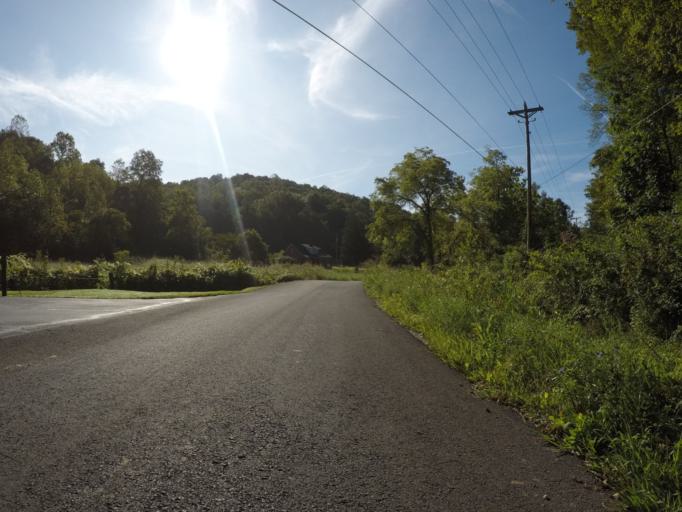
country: US
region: Ohio
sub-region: Lawrence County
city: Burlington
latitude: 38.5087
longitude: -82.5222
